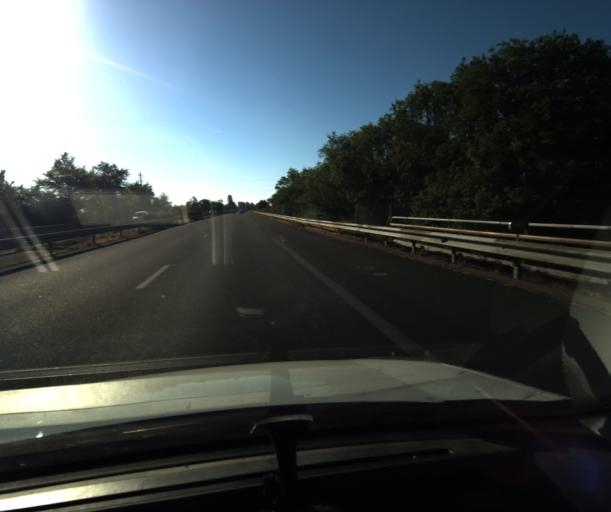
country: FR
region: Midi-Pyrenees
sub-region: Departement du Tarn-et-Garonne
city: Castelsarrasin
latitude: 44.0549
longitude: 1.1252
